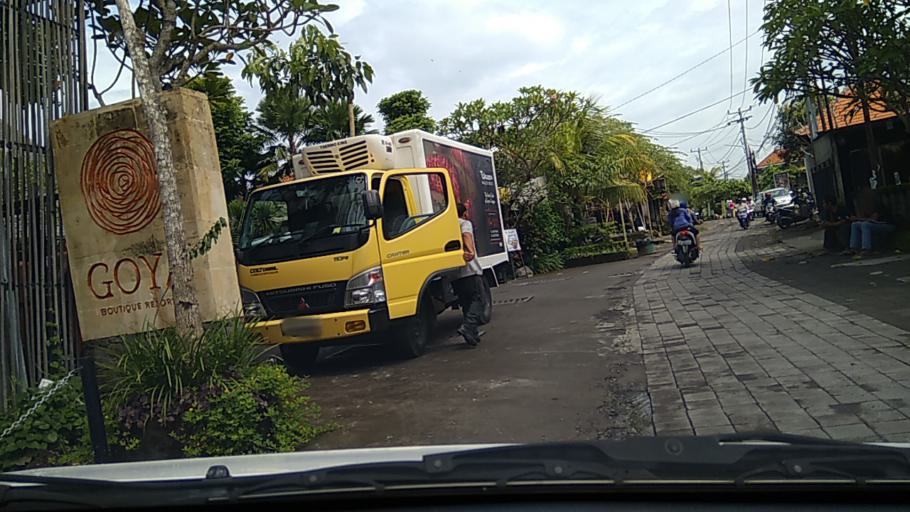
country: ID
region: Bali
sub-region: Kabupaten Gianyar
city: Ubud
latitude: -8.5122
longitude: 115.2583
